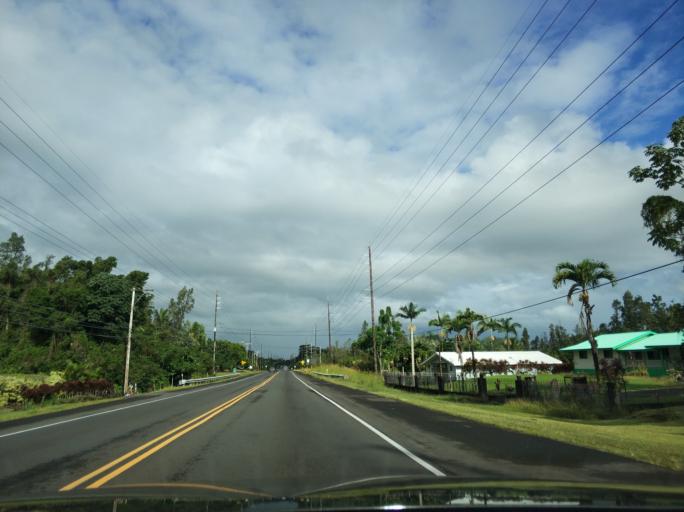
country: US
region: Hawaii
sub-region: Hawaii County
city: Orchidlands Estates
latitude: 19.5643
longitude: -154.9951
